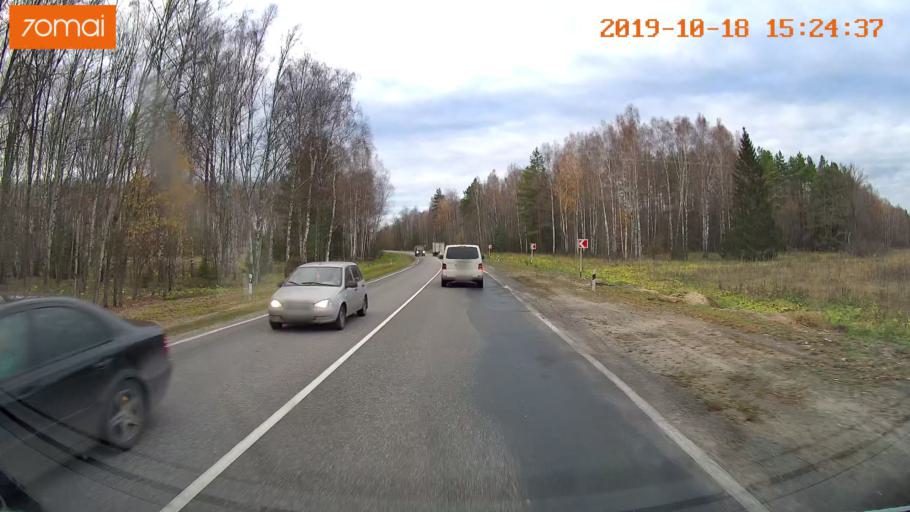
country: RU
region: Vladimir
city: Anopino
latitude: 55.7360
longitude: 40.7204
